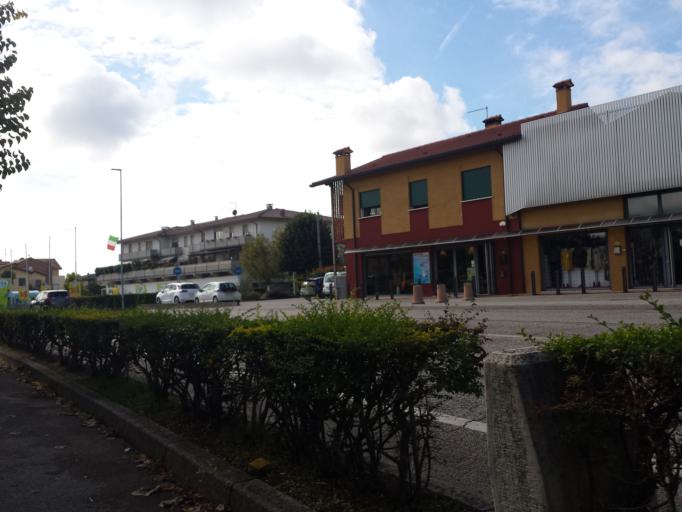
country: IT
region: Veneto
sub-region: Provincia di Vicenza
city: Sandrigo
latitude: 45.6615
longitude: 11.5929
